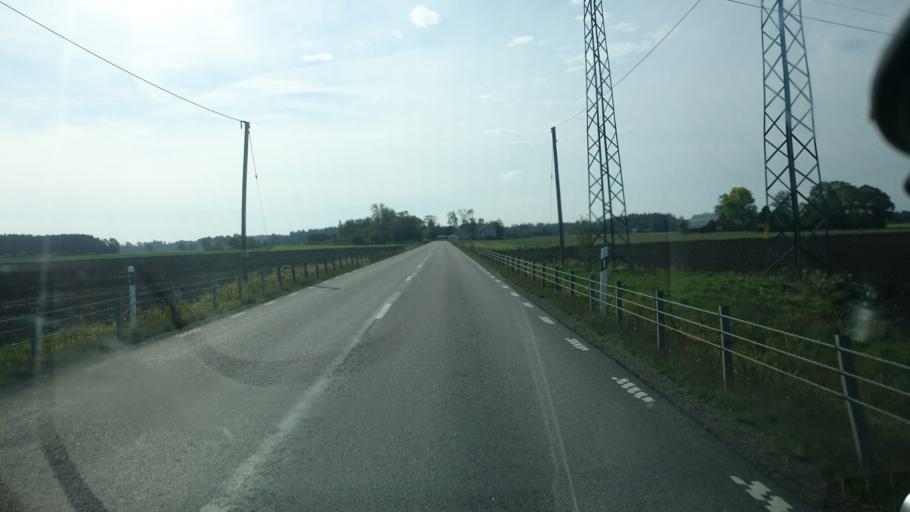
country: SE
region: Vaestra Goetaland
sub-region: Vanersborgs Kommun
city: Vargon
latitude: 58.2716
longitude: 12.3997
